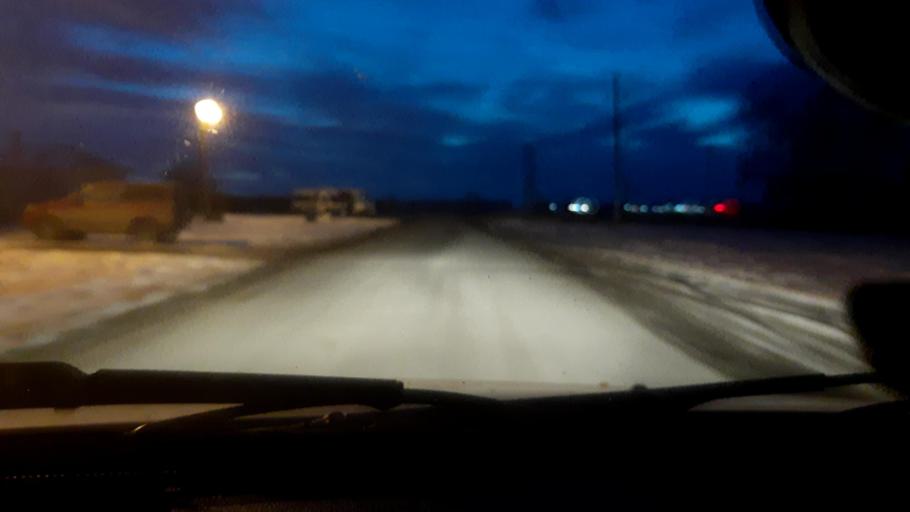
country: RU
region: Bashkortostan
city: Avdon
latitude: 54.7030
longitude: 55.7876
